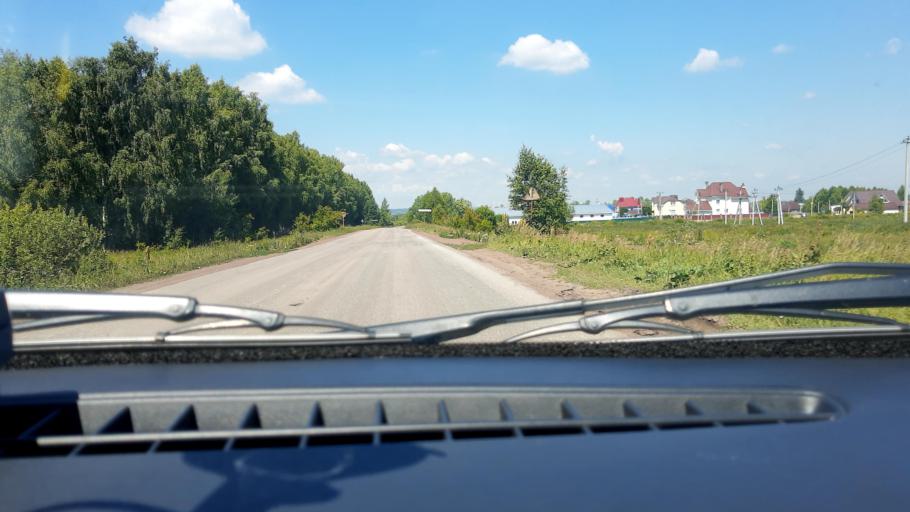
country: RU
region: Bashkortostan
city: Kabakovo
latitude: 54.6777
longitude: 56.1367
